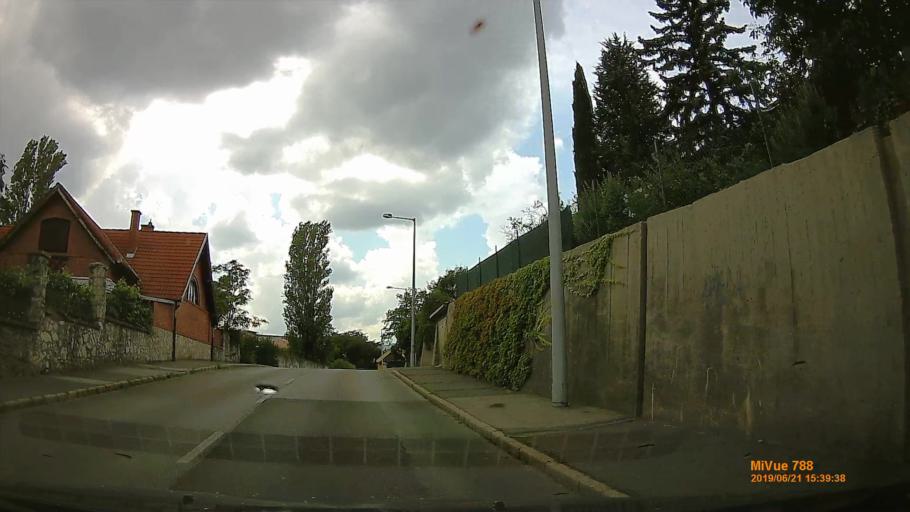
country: HU
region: Baranya
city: Pecs
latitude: 46.0802
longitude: 18.2180
